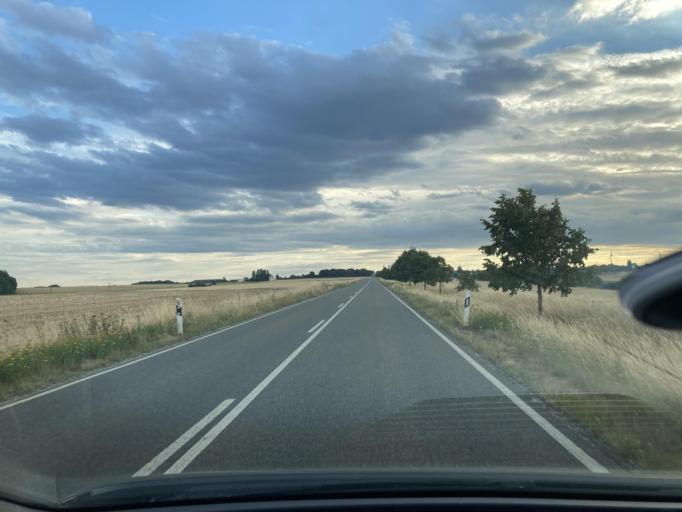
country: DE
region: Rheinland-Pfalz
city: Rodern
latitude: 49.9508
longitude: 7.4357
